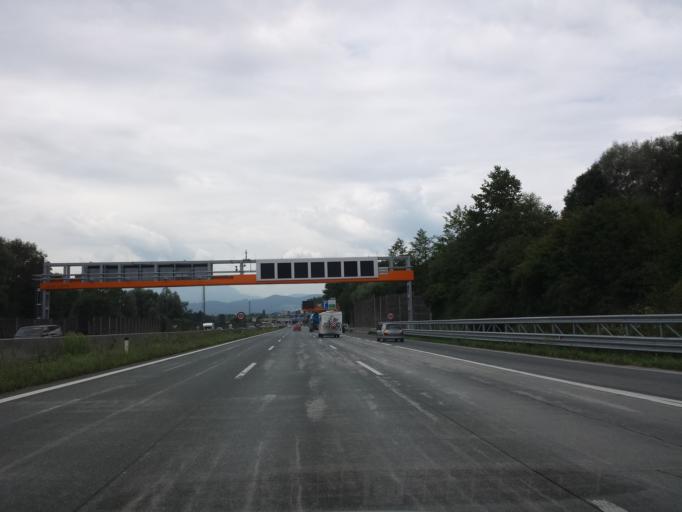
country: AT
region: Salzburg
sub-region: Politischer Bezirk Salzburg-Umgebung
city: Bergheim
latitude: 47.8274
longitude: 13.0272
